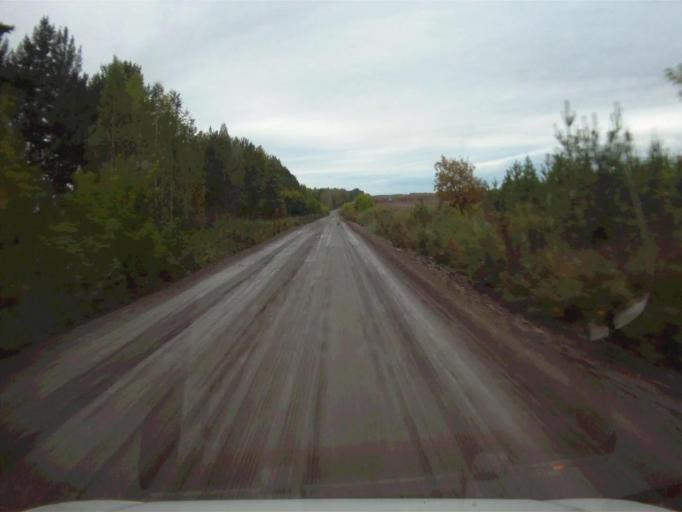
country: RU
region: Sverdlovsk
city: Mikhaylovsk
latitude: 56.1469
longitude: 59.2787
